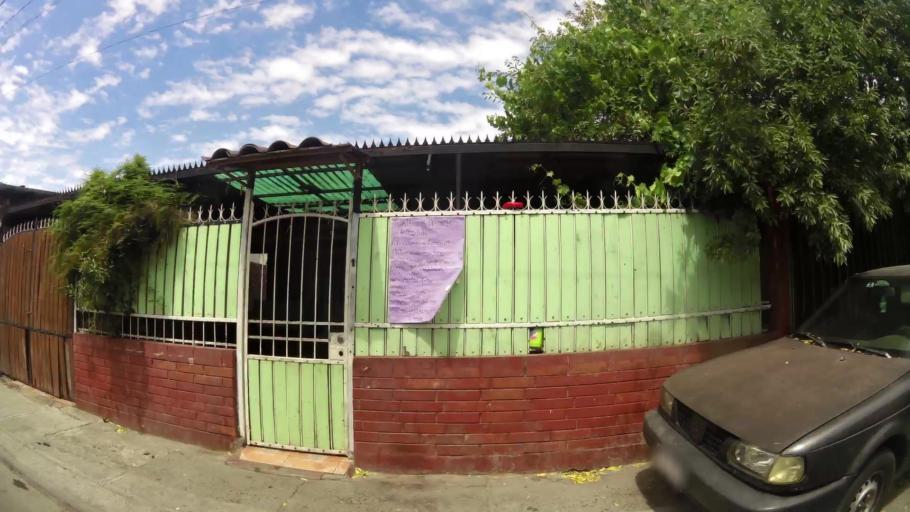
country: CL
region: Santiago Metropolitan
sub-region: Provincia de Santiago
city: La Pintana
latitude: -33.5849
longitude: -70.6496
